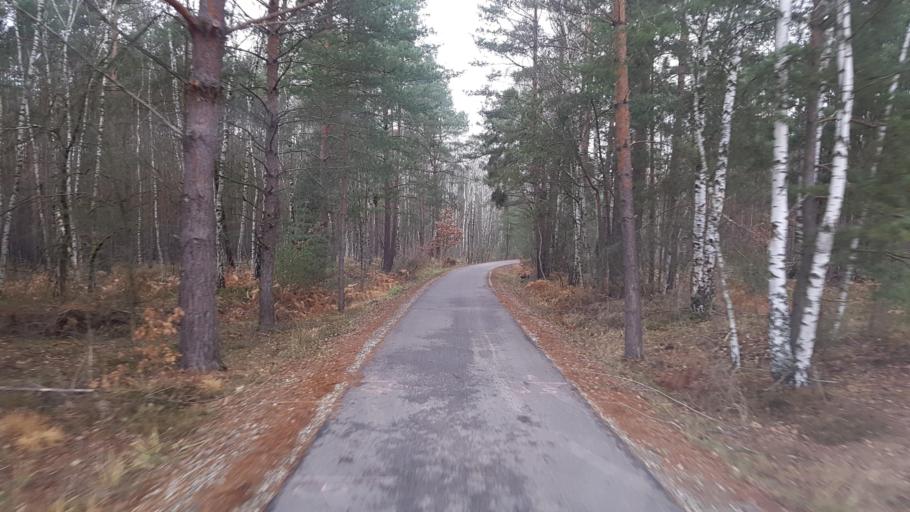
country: DE
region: Brandenburg
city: Plessa
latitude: 51.5177
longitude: 13.6776
